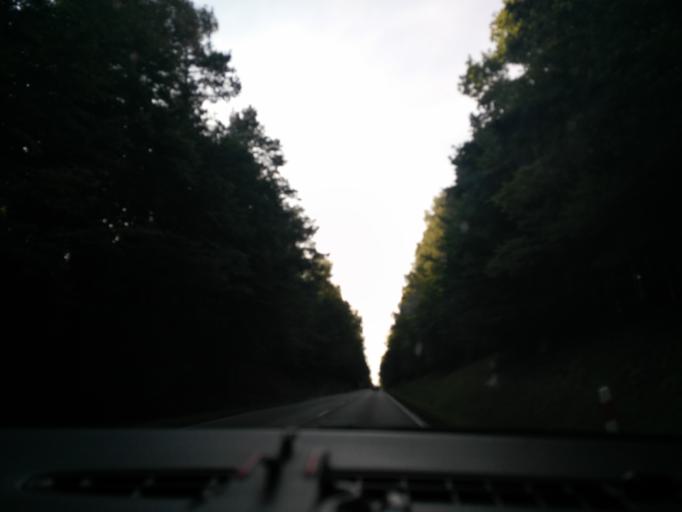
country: PL
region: Lublin Voivodeship
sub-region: Powiat krasnicki
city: Szastarka
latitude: 50.8556
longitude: 22.2845
